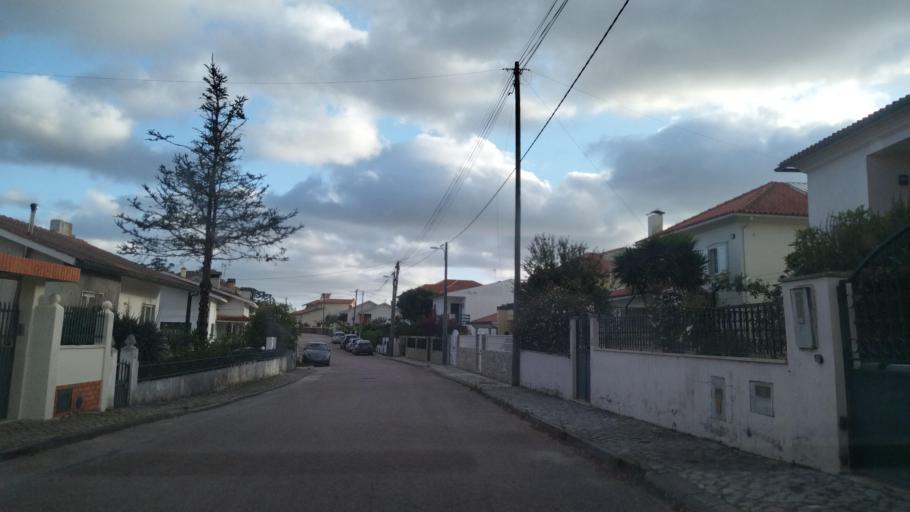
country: PT
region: Coimbra
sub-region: Coimbra
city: Coimbra
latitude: 40.1731
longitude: -8.4427
